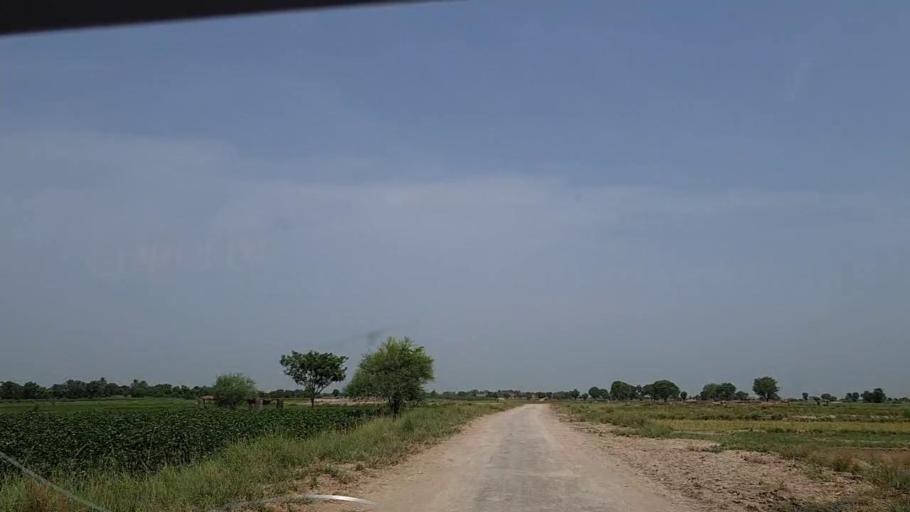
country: PK
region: Sindh
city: Tharu Shah
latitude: 26.9155
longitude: 68.0564
